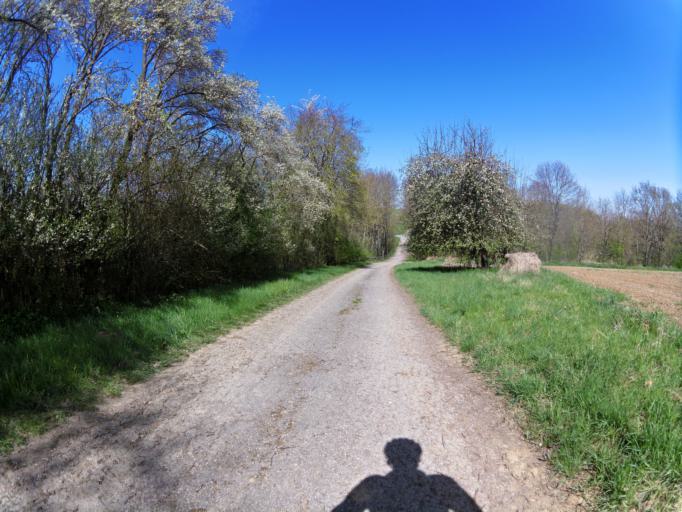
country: DE
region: Bavaria
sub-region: Regierungsbezirk Unterfranken
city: Winterhausen
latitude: 49.6979
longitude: 9.9963
